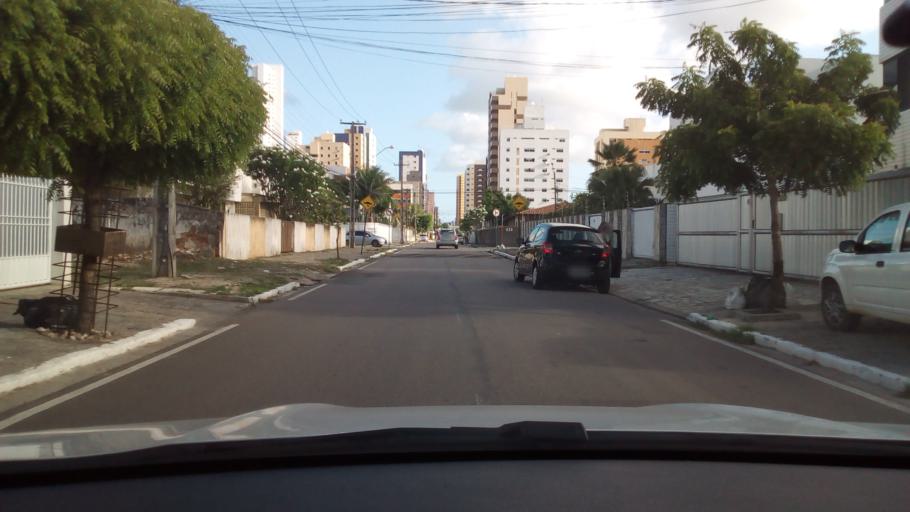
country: BR
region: Paraiba
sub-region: Joao Pessoa
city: Joao Pessoa
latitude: -7.1029
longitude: -34.8396
